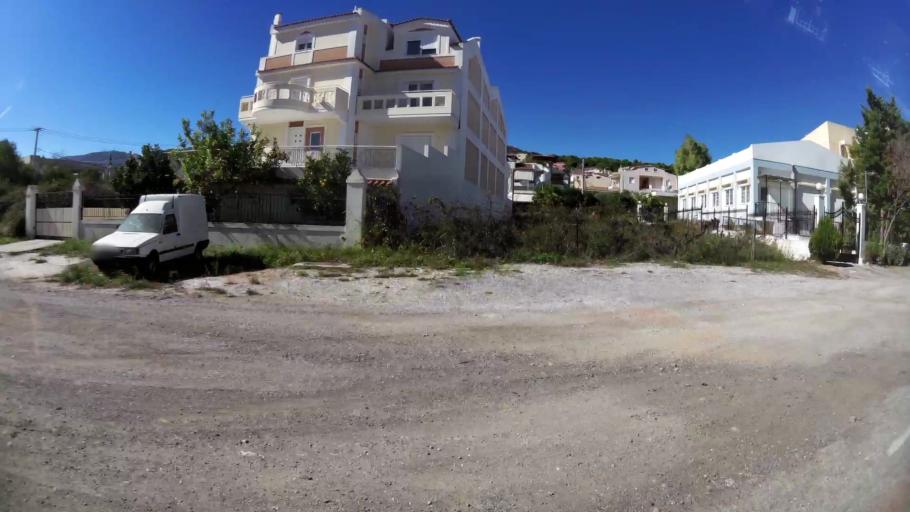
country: GR
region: Attica
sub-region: Nomarchia Anatolikis Attikis
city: Leondarion
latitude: 38.0036
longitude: 23.8539
